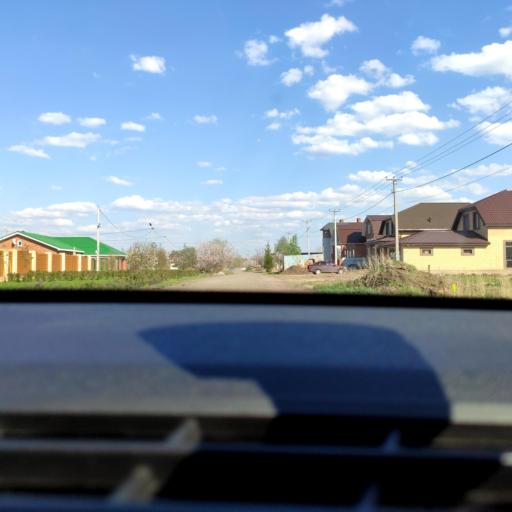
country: RU
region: Samara
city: Tol'yatti
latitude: 53.5552
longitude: 49.3767
